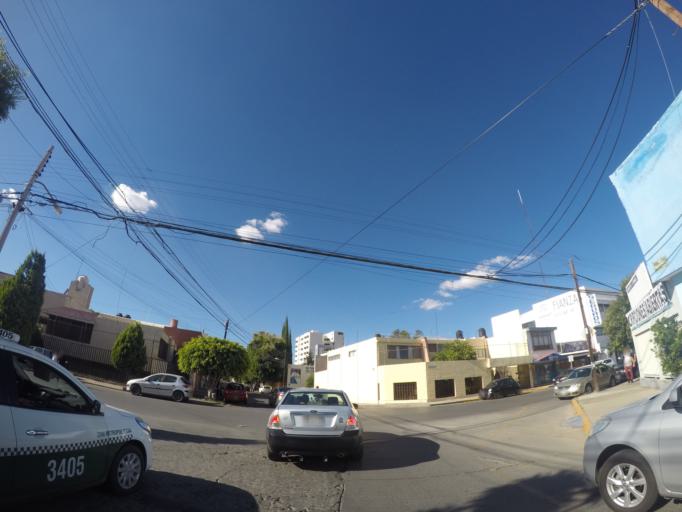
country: MX
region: San Luis Potosi
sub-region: San Luis Potosi
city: San Luis Potosi
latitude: 22.1475
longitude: -101.0018
